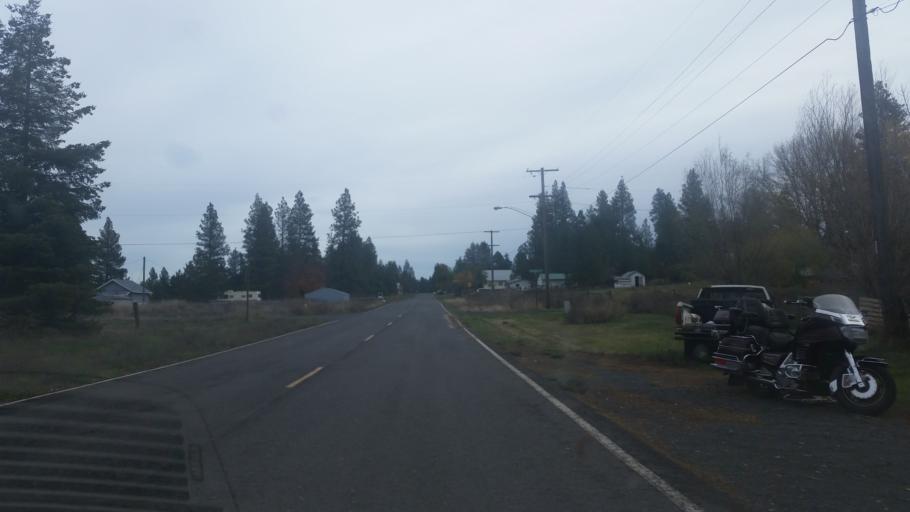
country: US
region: Washington
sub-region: Spokane County
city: Cheney
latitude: 47.2286
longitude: -117.4796
